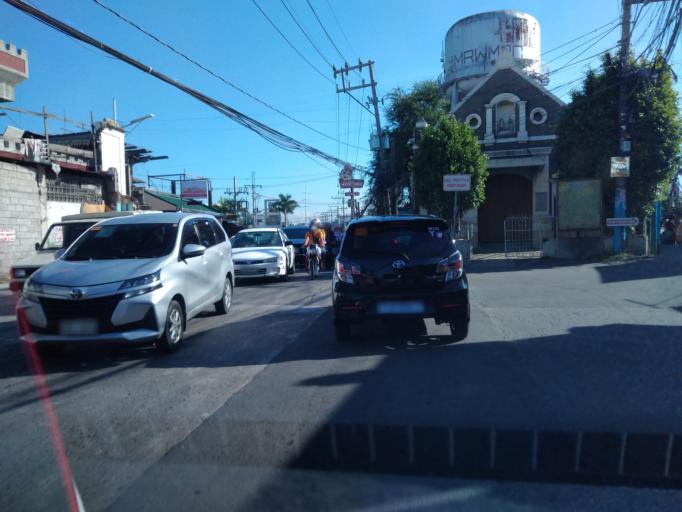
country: PH
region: Central Luzon
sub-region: Province of Bulacan
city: Meycauayan
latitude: 14.7427
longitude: 120.9701
